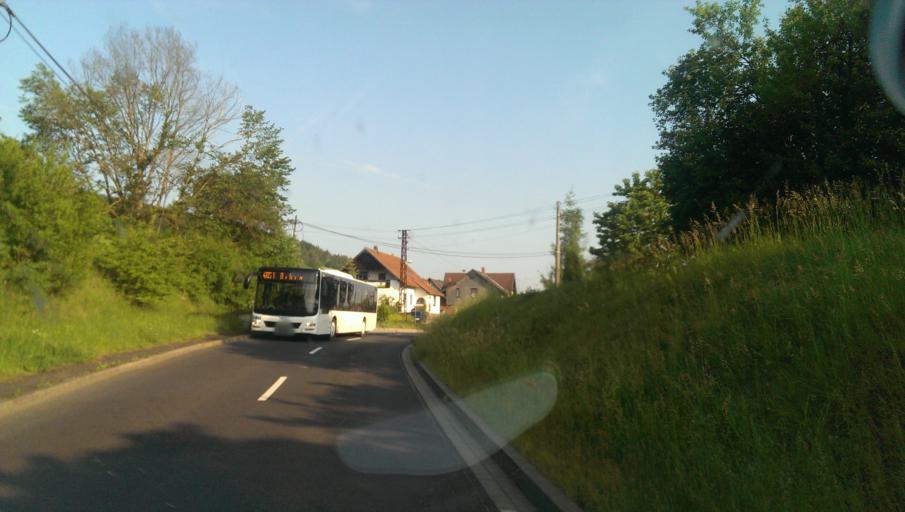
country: DE
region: Thuringia
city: Ritschenhausen
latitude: 50.5086
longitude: 10.4337
